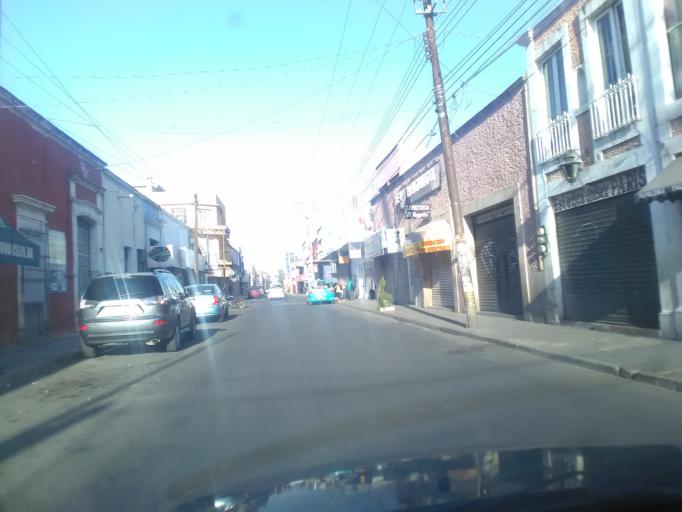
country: MX
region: Durango
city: Victoria de Durango
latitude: 24.0227
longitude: -104.6666
